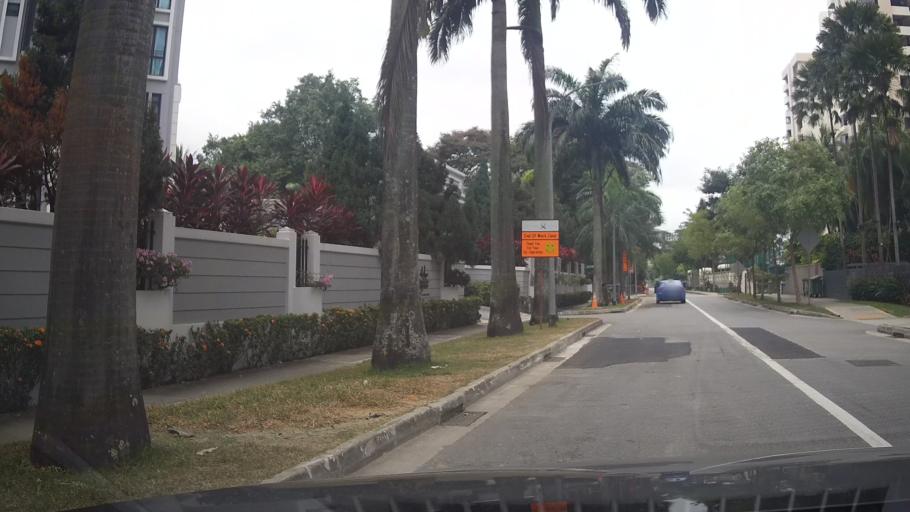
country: SG
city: Singapore
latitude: 1.2986
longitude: 103.8874
